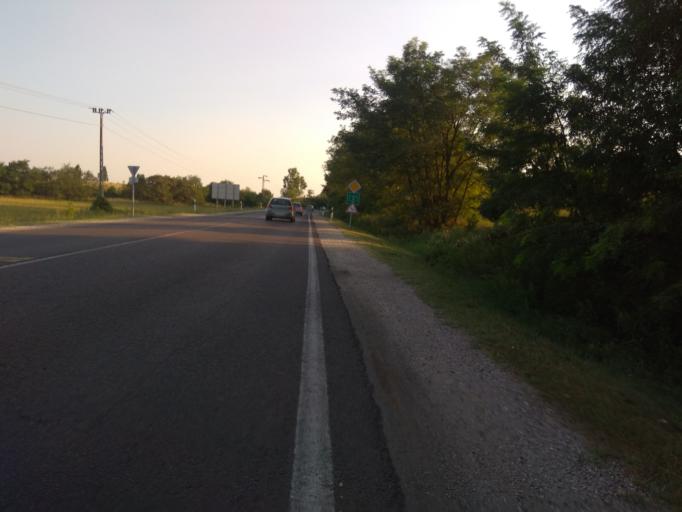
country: HU
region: Borsod-Abauj-Zemplen
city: Emod
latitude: 47.9419
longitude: 20.8290
